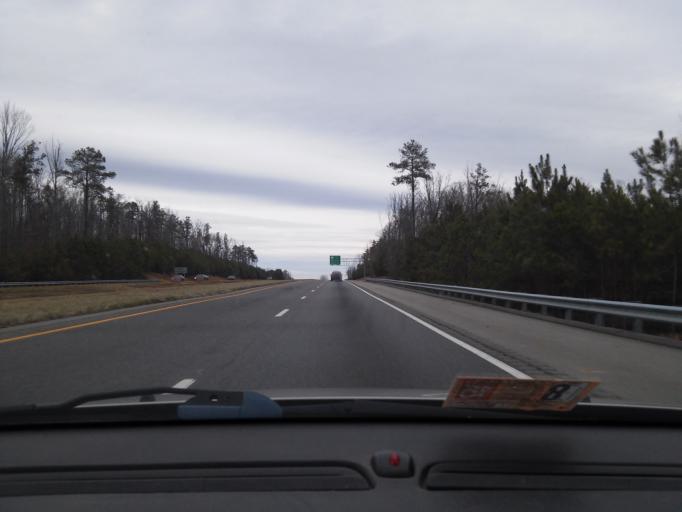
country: US
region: Virginia
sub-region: Henrico County
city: Short Pump
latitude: 37.5869
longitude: -77.6731
